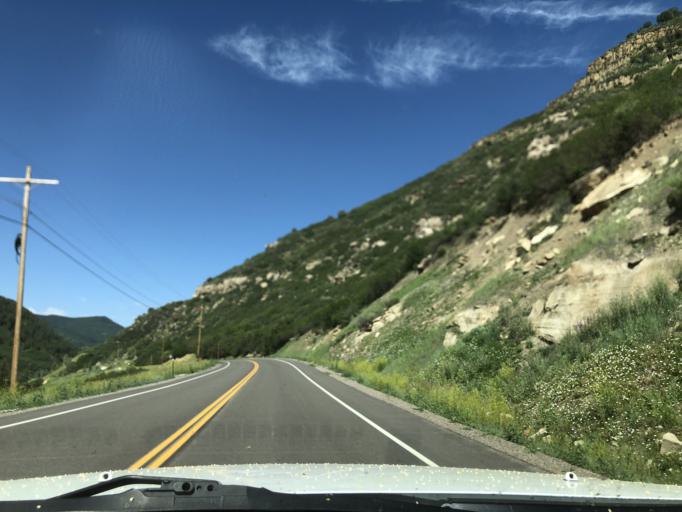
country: US
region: Colorado
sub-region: Delta County
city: Paonia
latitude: 38.9340
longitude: -107.3999
